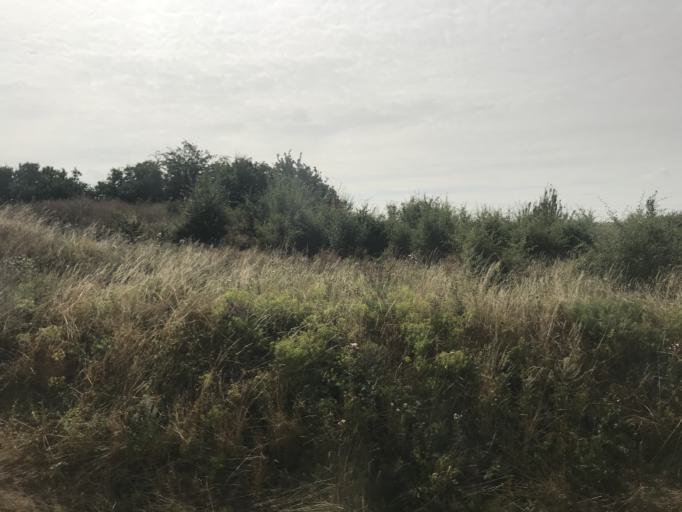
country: PL
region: Kujawsko-Pomorskie
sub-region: Powiat inowroclawski
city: Inowroclaw
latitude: 52.7835
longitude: 18.1887
